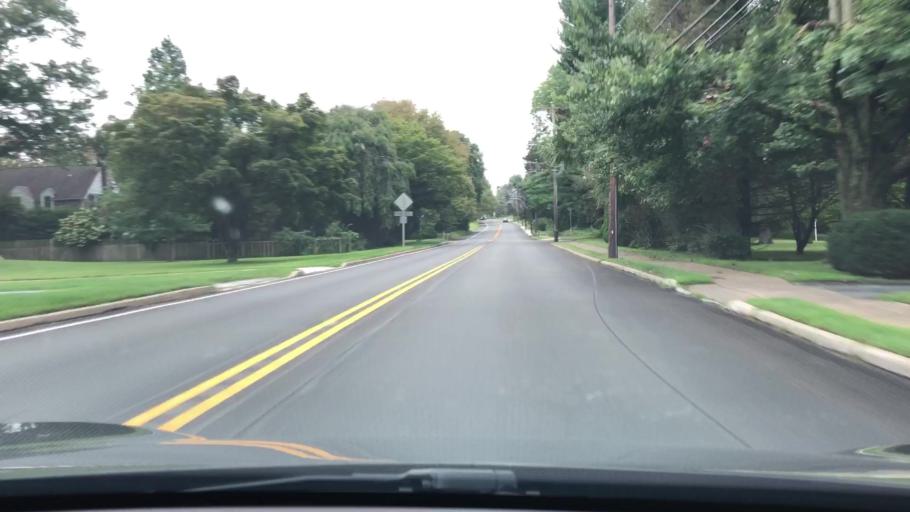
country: US
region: Pennsylvania
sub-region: Delaware County
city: Broomall
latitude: 39.9882
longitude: -75.3585
